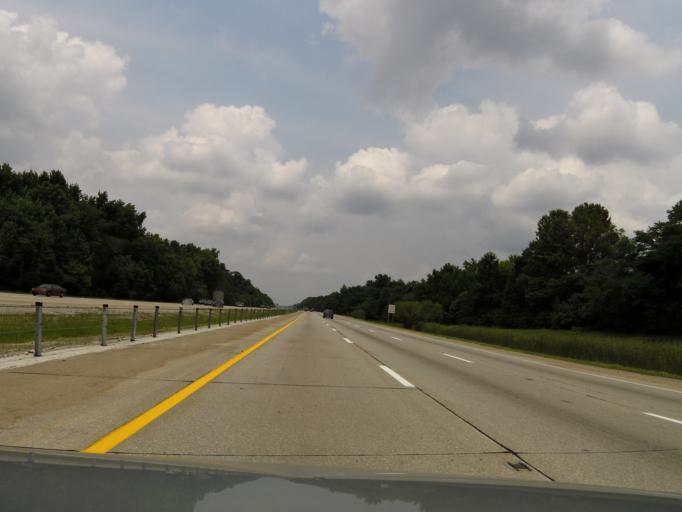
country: US
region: Kentucky
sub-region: Bullitt County
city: Hillview
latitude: 38.0930
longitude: -85.7008
